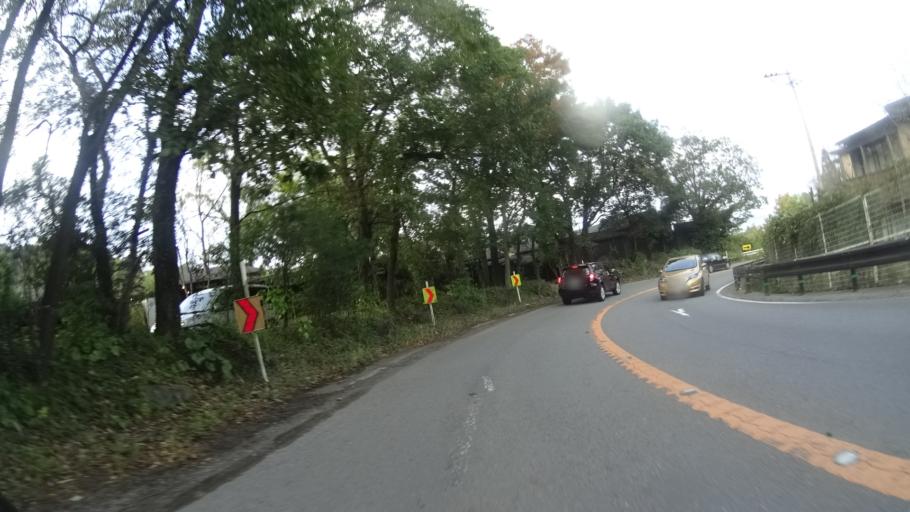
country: JP
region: Oita
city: Beppu
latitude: 33.2907
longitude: 131.4564
